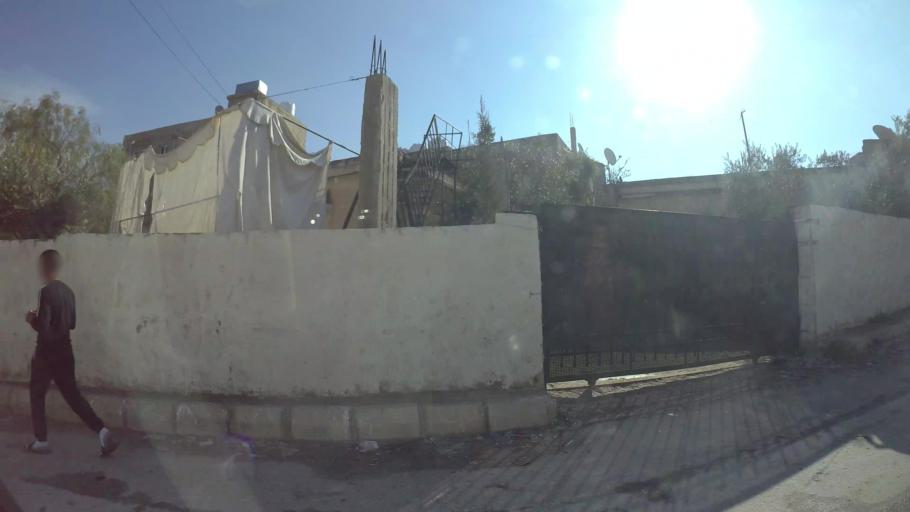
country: JO
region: Amman
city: Al Jubayhah
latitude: 32.0769
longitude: 35.8519
